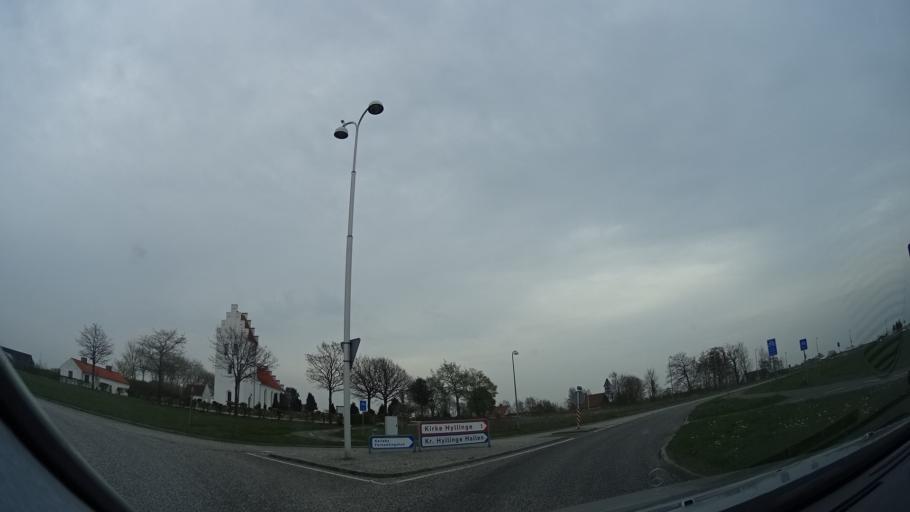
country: DK
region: Zealand
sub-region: Lejre Kommune
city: Ejby
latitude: 55.7036
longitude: 11.8868
